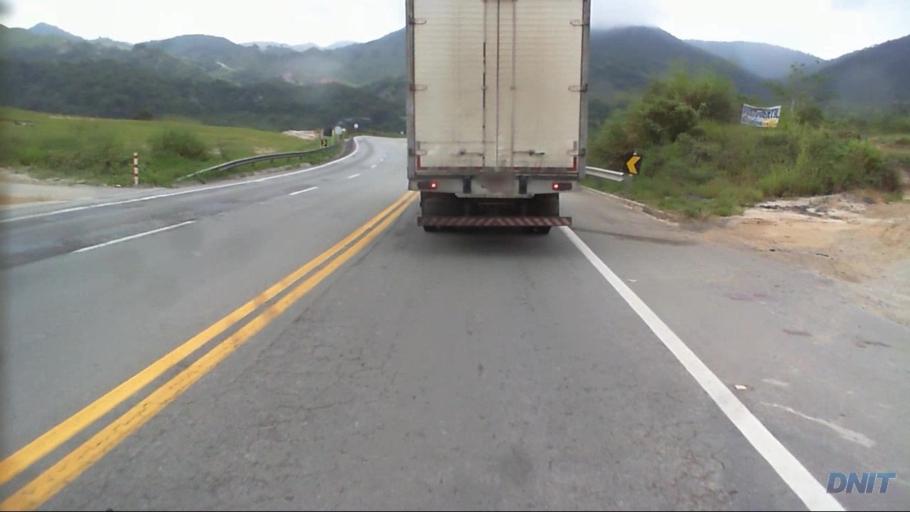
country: BR
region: Minas Gerais
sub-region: Nova Era
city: Nova Era
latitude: -19.6524
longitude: -42.9505
